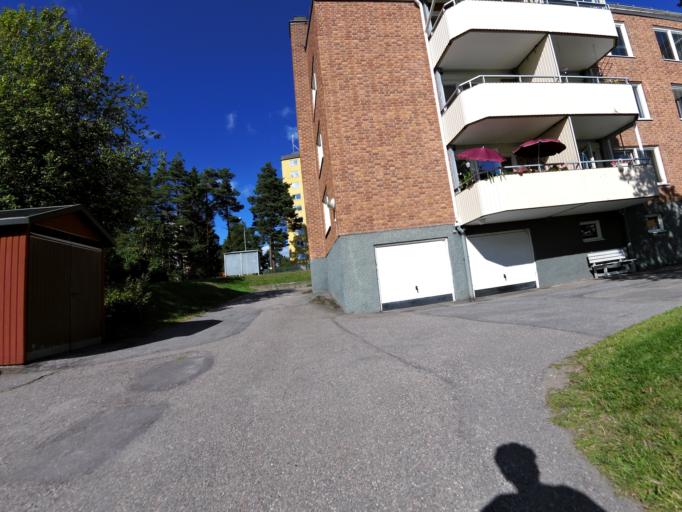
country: SE
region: Gaevleborg
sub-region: Gavle Kommun
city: Gavle
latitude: 60.6952
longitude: 17.1487
